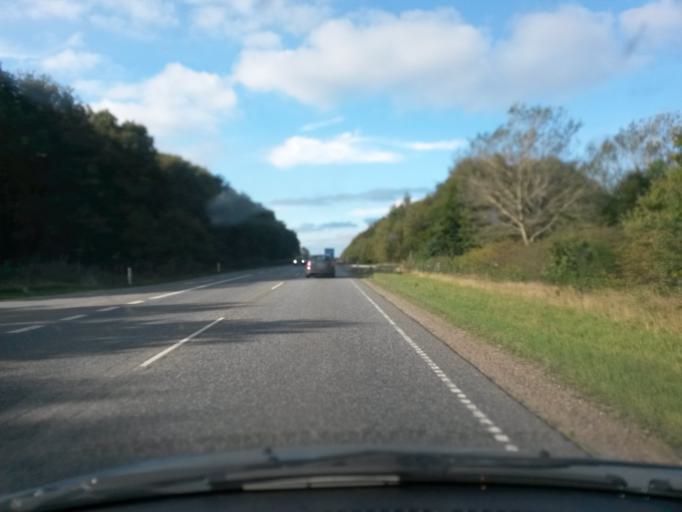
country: DK
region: Central Jutland
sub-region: Herning Kommune
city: Avlum
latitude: 56.2855
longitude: 8.7442
